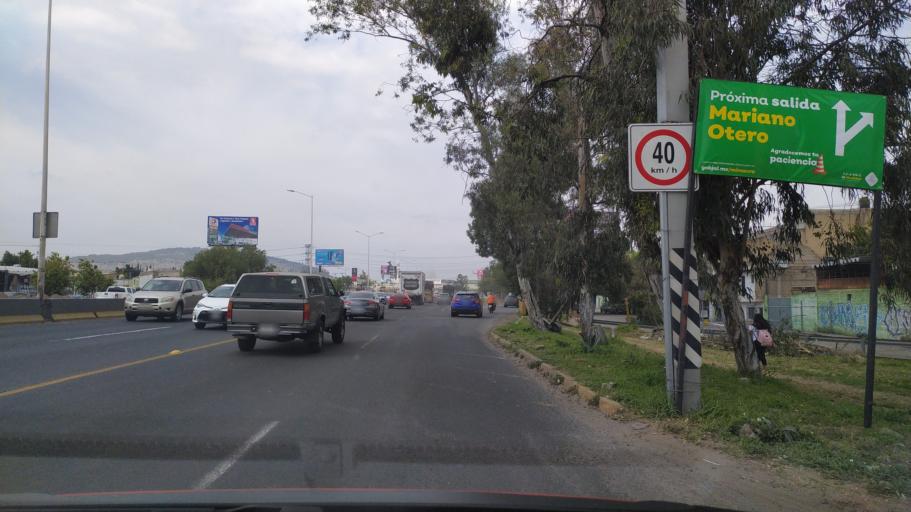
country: MX
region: Jalisco
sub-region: Tlajomulco de Zuniga
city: Palomar
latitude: 20.6262
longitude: -103.4340
